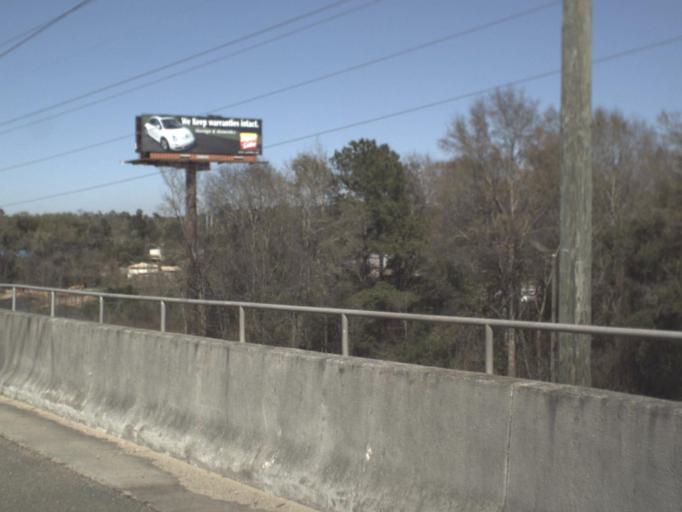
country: US
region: Florida
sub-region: Leon County
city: Tallahassee
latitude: 30.4538
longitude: -84.2264
